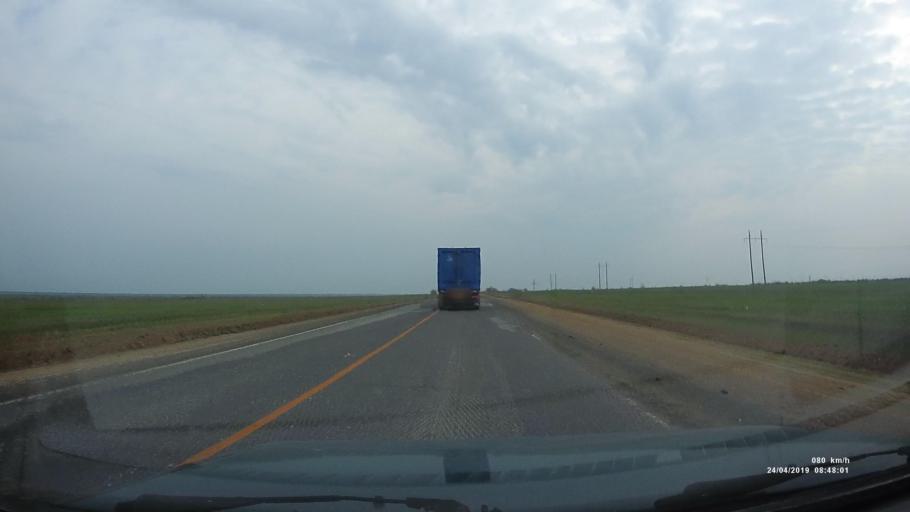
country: RU
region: Kalmykiya
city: Arshan'
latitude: 46.2486
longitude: 44.1026
